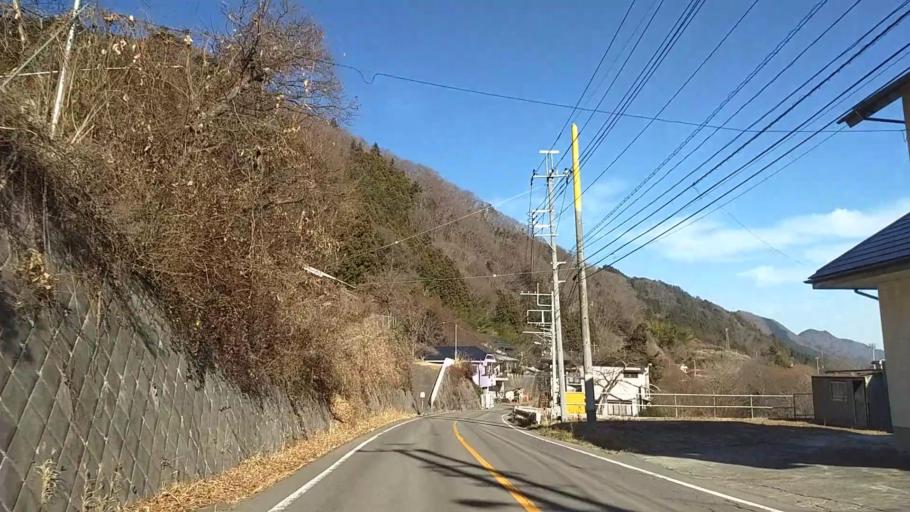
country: JP
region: Yamanashi
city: Otsuki
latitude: 35.5258
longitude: 139.0262
